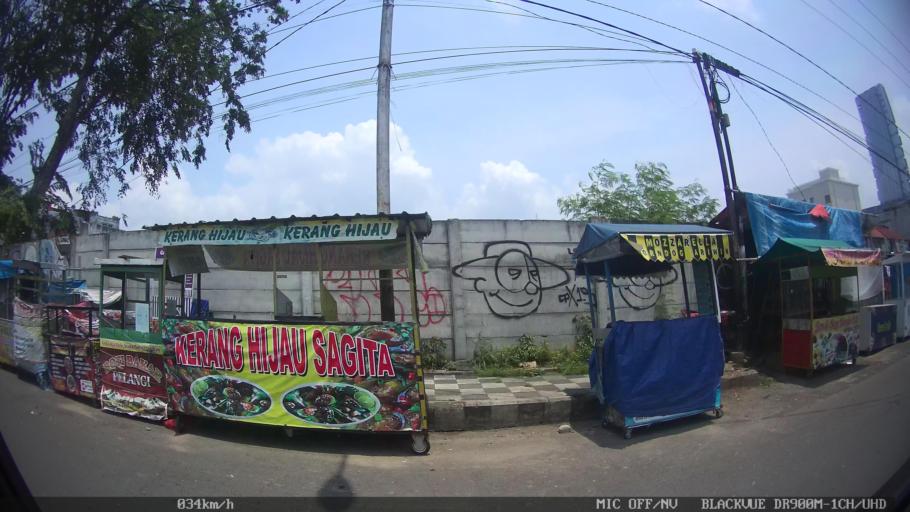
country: ID
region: Lampung
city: Bandarlampung
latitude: -5.4211
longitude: 105.2594
